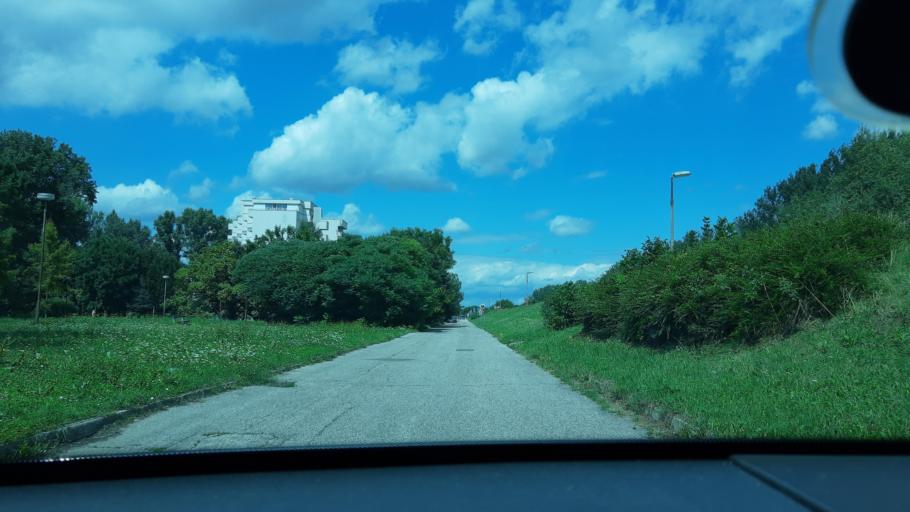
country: SK
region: Trnavsky
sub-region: Okres Trnava
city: Piestany
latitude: 48.5936
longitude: 17.8405
